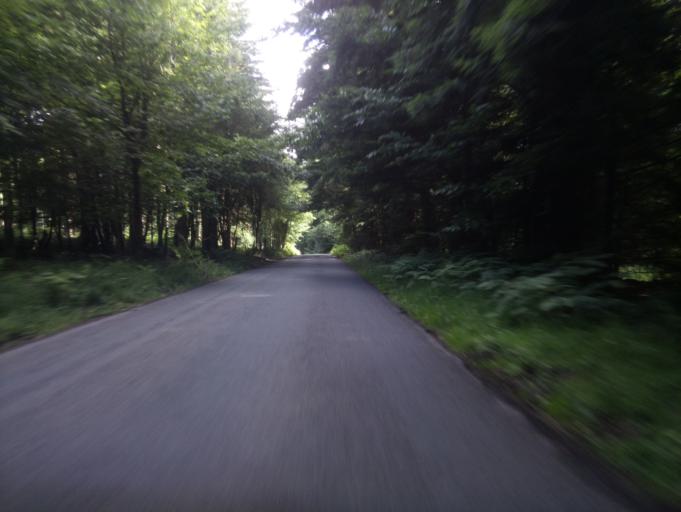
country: GB
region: England
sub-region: Gloucestershire
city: Cinderford
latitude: 51.7969
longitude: -2.4942
